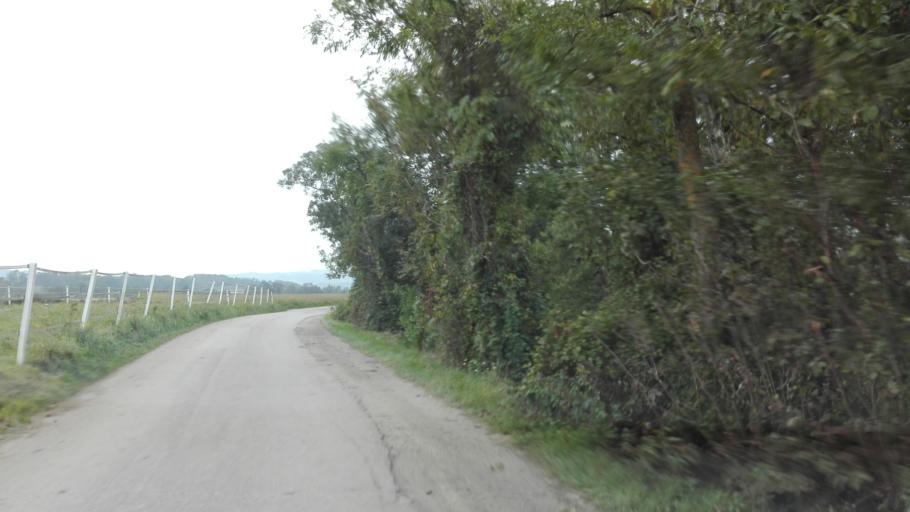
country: AT
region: Upper Austria
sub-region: Wels-Land
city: Buchkirchen
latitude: 48.2843
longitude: 14.0168
